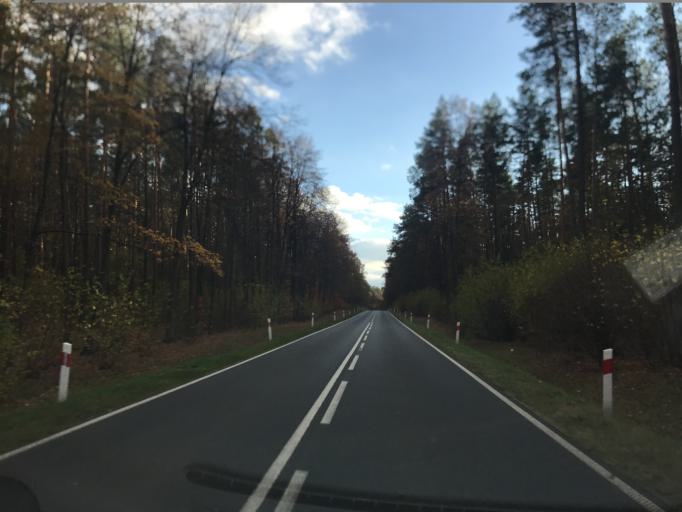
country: PL
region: Warmian-Masurian Voivodeship
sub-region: Powiat dzialdowski
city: Lidzbark
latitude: 53.3204
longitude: 19.8154
